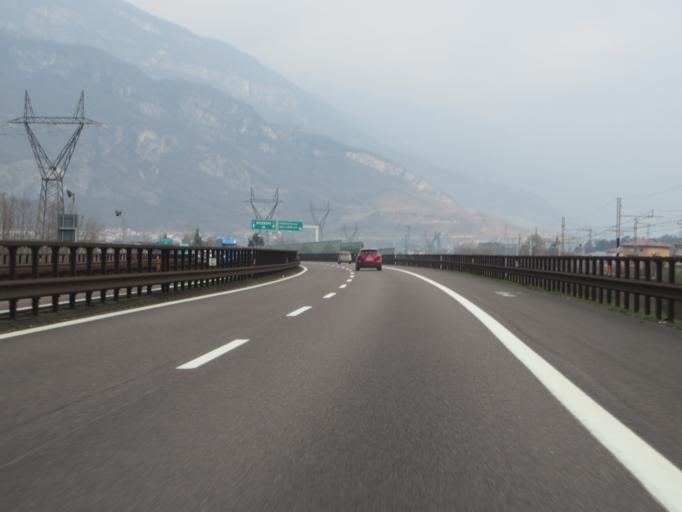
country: IT
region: Trentino-Alto Adige
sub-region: Provincia di Trento
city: Marco
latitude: 45.8374
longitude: 11.0029
